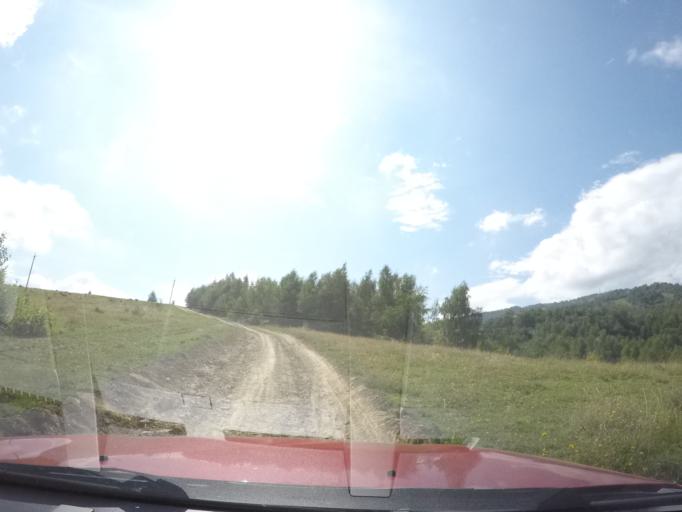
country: UA
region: Zakarpattia
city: Velykyi Bereznyi
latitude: 48.9468
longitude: 22.6672
